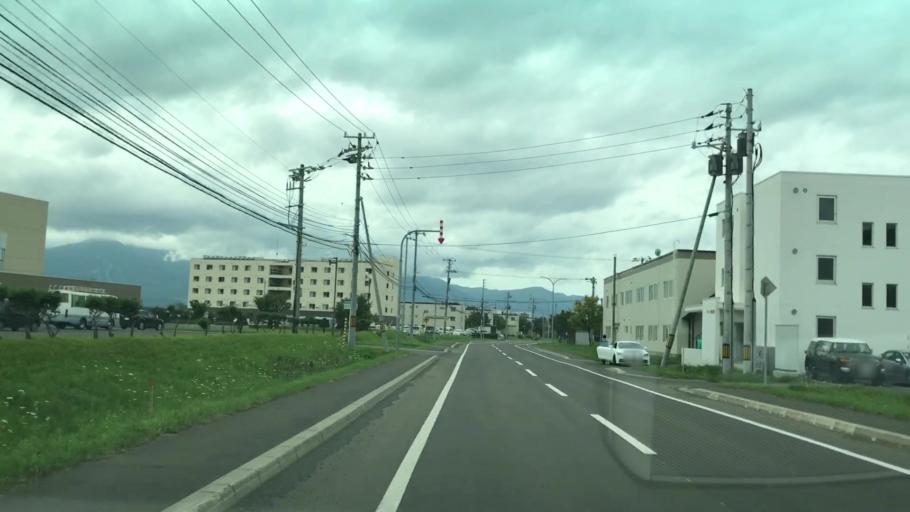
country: JP
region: Hokkaido
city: Iwanai
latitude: 43.0353
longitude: 140.5407
